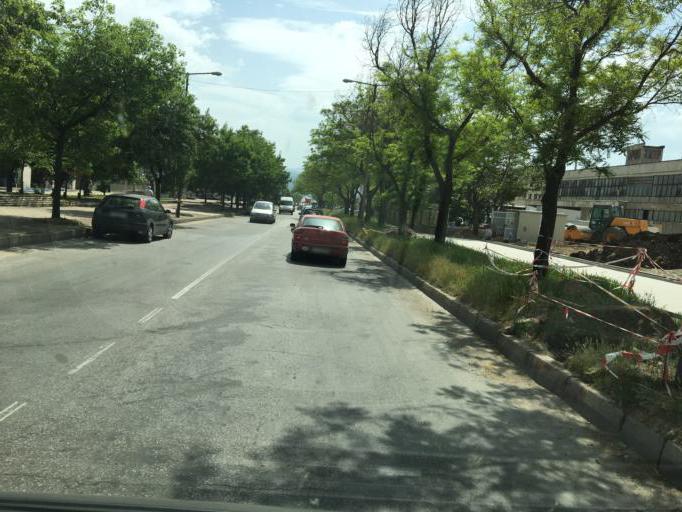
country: BG
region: Blagoevgrad
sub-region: Obshtina Blagoevgrad
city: Blagoevgrad
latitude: 42.0084
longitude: 23.0862
